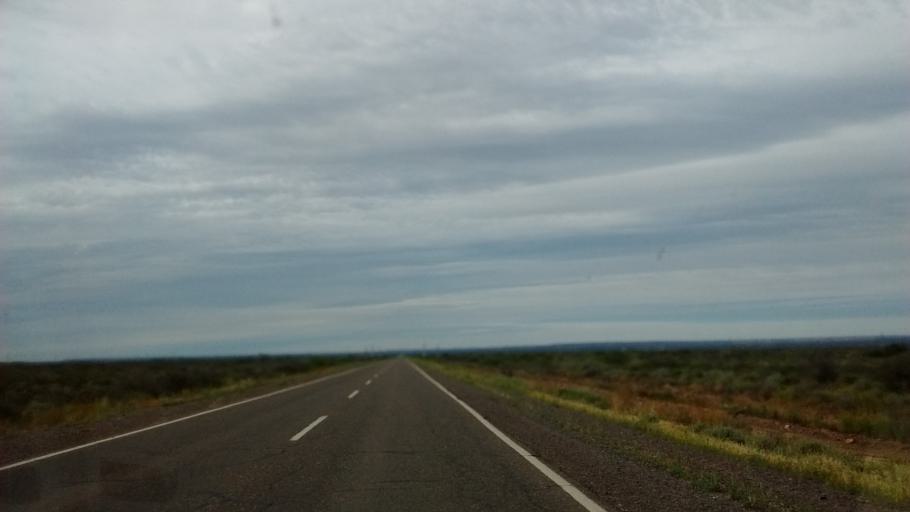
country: AR
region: Rio Negro
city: Catriel
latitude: -38.0033
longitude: -67.9119
